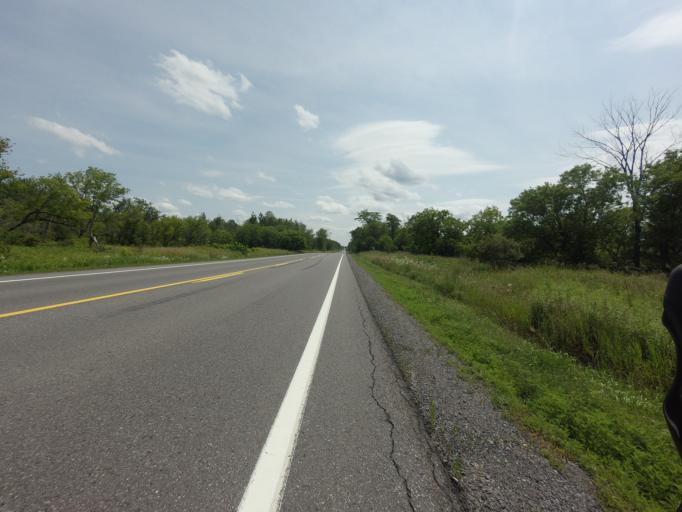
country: CA
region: Ontario
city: Ottawa
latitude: 45.3061
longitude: -75.6432
